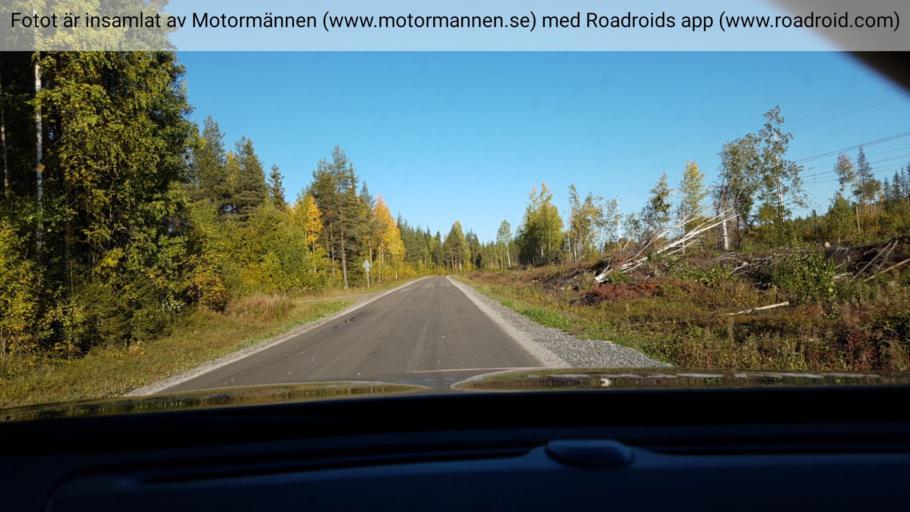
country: SE
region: Norrbotten
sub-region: Alvsbyns Kommun
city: AElvsbyn
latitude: 66.2014
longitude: 21.1788
